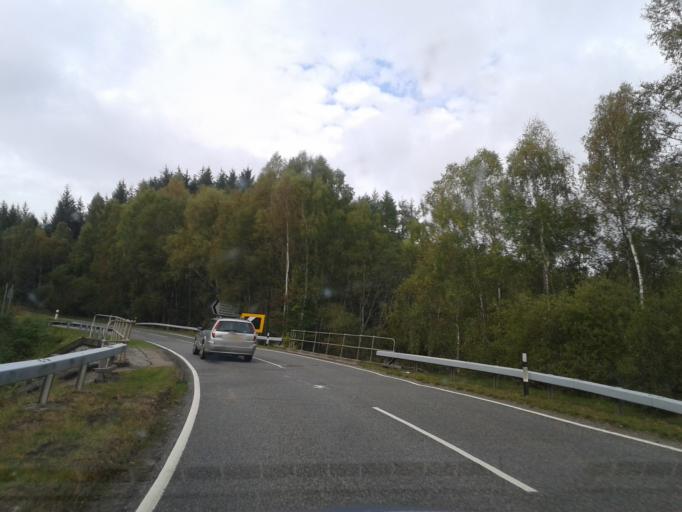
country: GB
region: Scotland
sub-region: Highland
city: Spean Bridge
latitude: 57.0834
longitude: -4.9002
